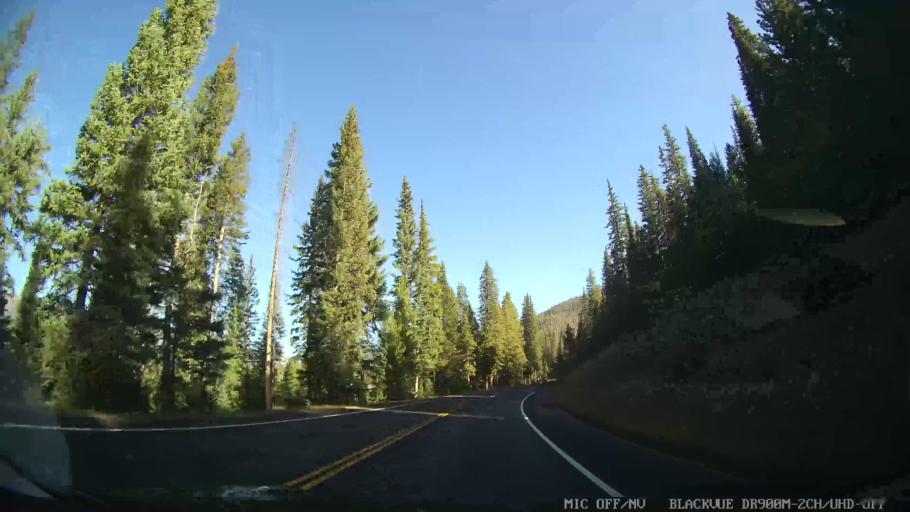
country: US
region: Colorado
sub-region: Grand County
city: Granby
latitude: 40.3048
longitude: -105.8428
